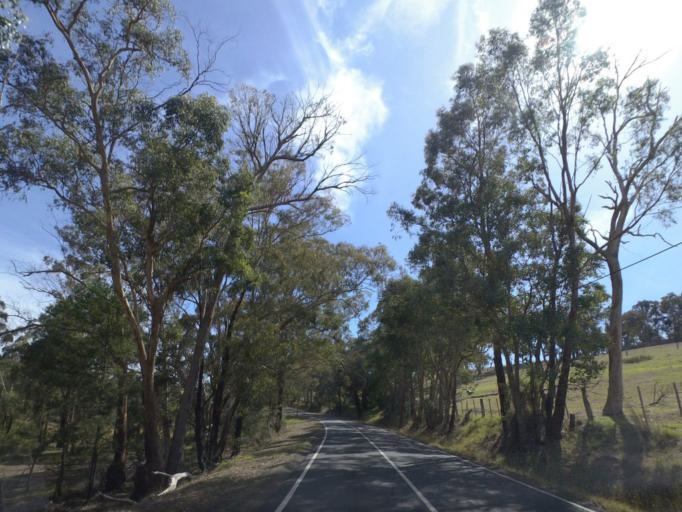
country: AU
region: Victoria
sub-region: Nillumbik
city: Hurstbridge
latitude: -37.6150
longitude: 145.2286
